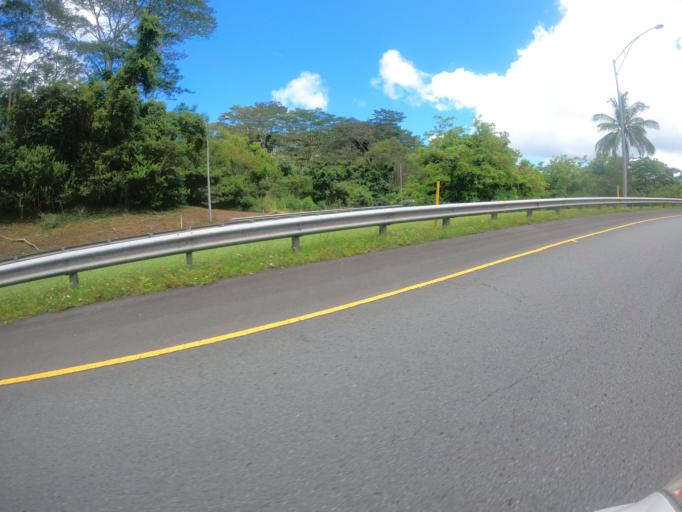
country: US
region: Hawaii
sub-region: Honolulu County
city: Maunawili
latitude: 21.3860
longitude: -157.7894
